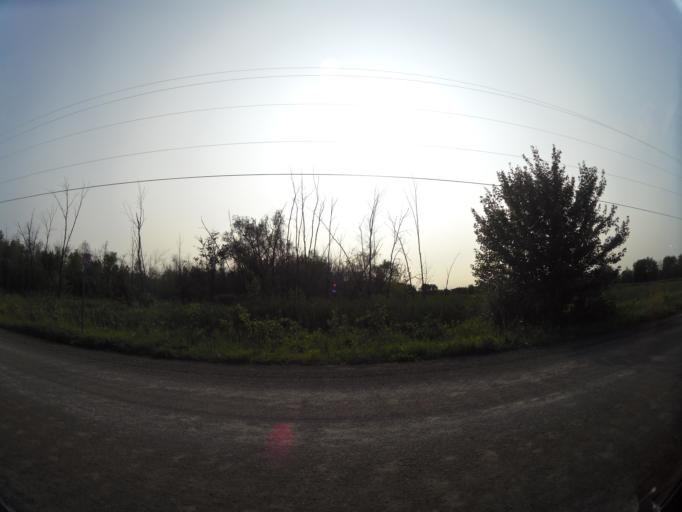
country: CA
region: Ontario
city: Clarence-Rockland
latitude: 45.4983
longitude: -75.4838
